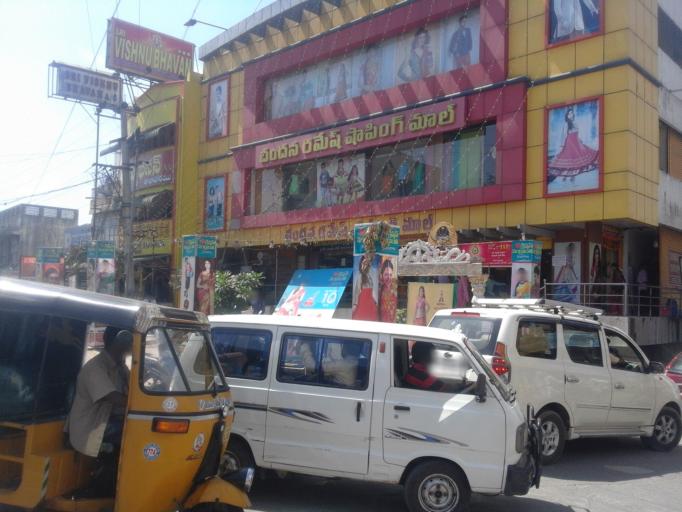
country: IN
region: Andhra Pradesh
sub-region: Chittoor
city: Chittoor
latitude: 13.2189
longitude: 79.1011
